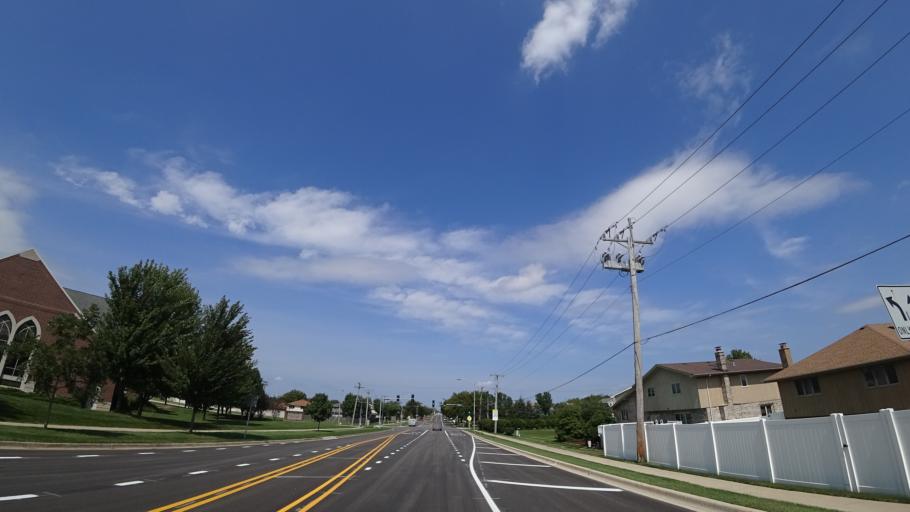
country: US
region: Illinois
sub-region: Cook County
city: Orland Hills
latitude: 41.5718
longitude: -87.8224
